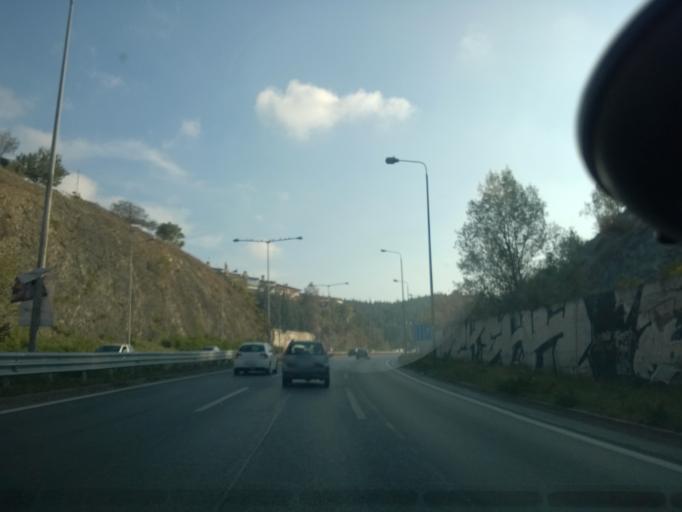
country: GR
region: Central Macedonia
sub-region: Nomos Thessalonikis
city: Polichni
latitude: 40.6623
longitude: 22.9677
